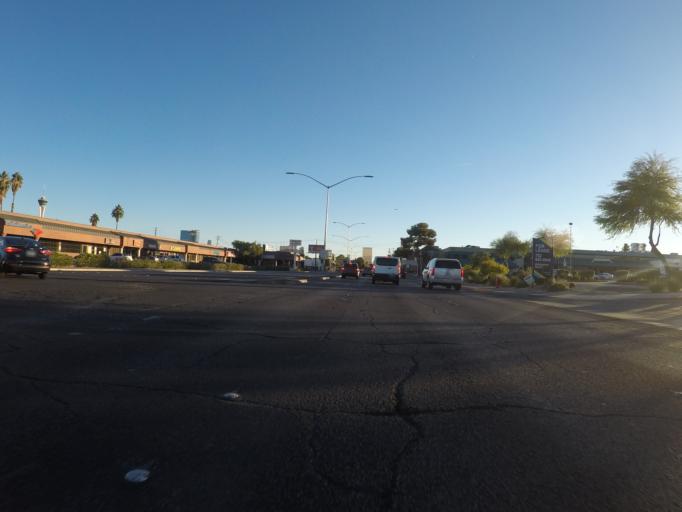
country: US
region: Nevada
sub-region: Clark County
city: Las Vegas
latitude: 36.1611
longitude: -115.1728
